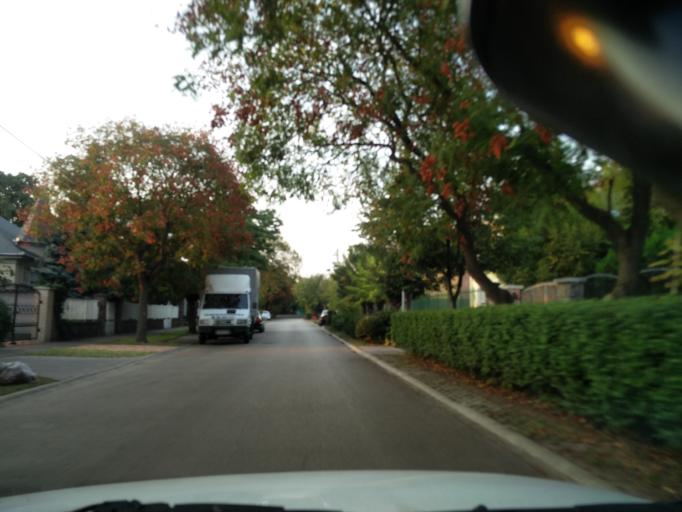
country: HU
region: Budapest
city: Budapest XXI. keruelet
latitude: 47.4236
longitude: 19.0735
